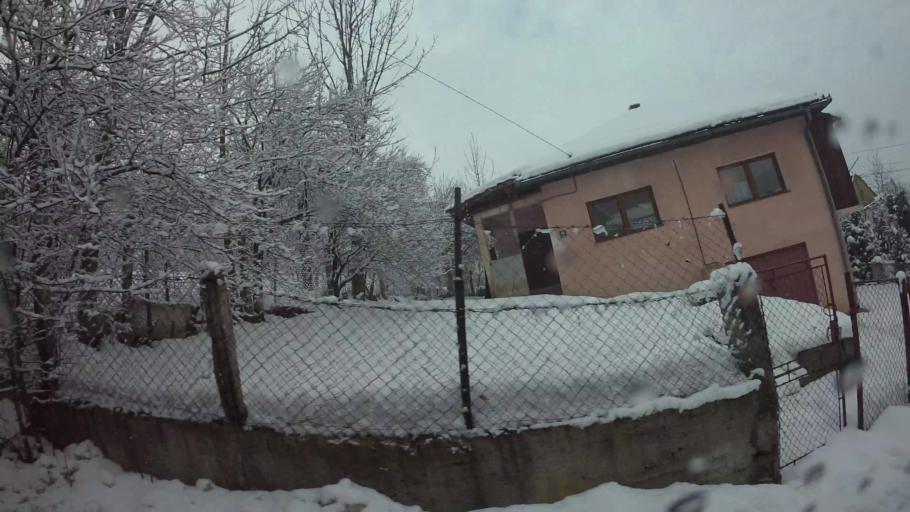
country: BA
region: Federation of Bosnia and Herzegovina
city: Kobilja Glava
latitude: 43.8481
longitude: 18.4254
